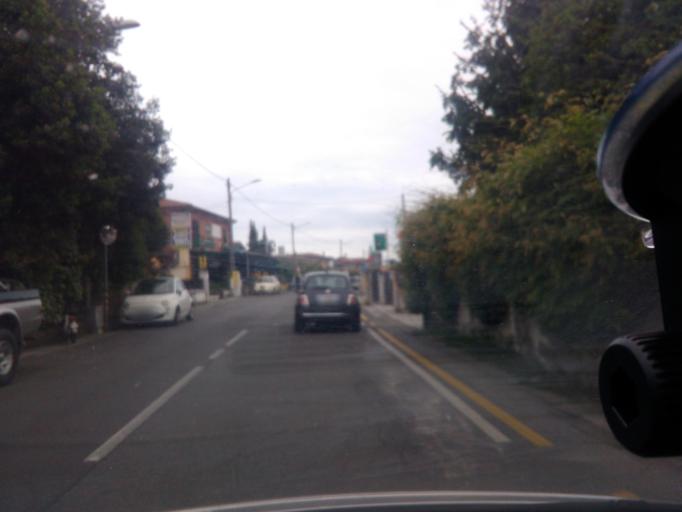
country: IT
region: Tuscany
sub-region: Provincia di Massa-Carrara
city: Massa
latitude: 44.0172
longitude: 10.1118
